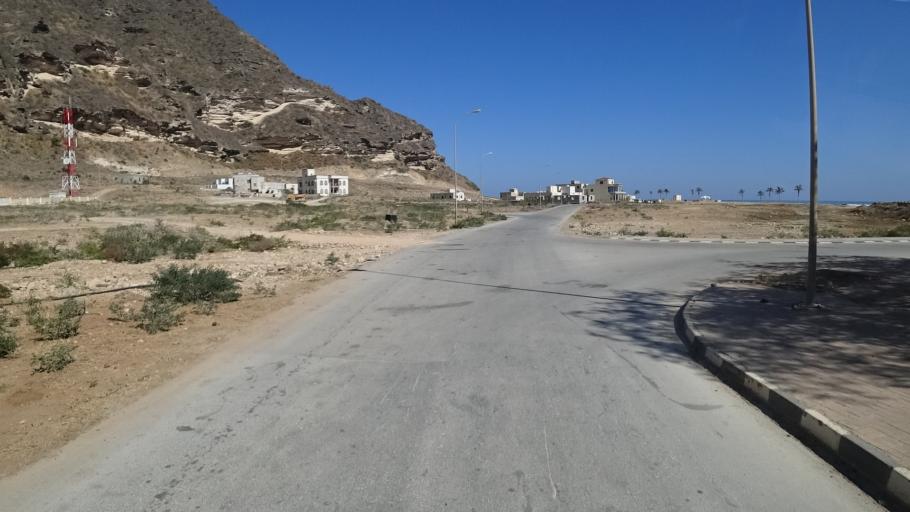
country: YE
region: Al Mahrah
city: Hawf
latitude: 16.7490
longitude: 53.4243
